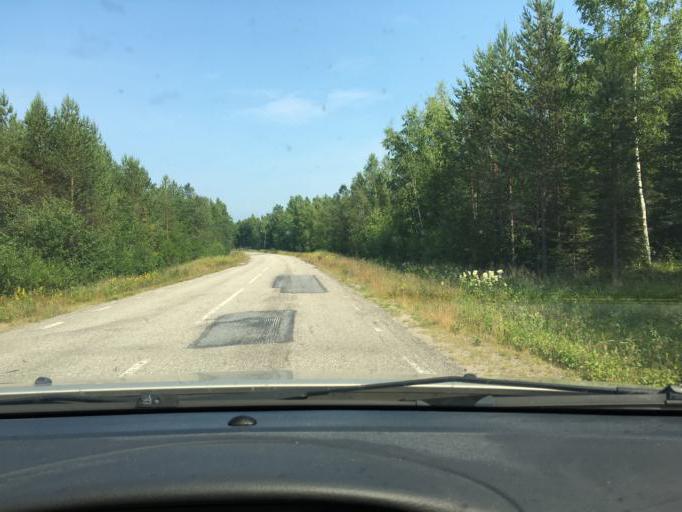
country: SE
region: Norrbotten
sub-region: Kalix Kommun
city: Kalix
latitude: 65.7785
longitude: 23.1972
